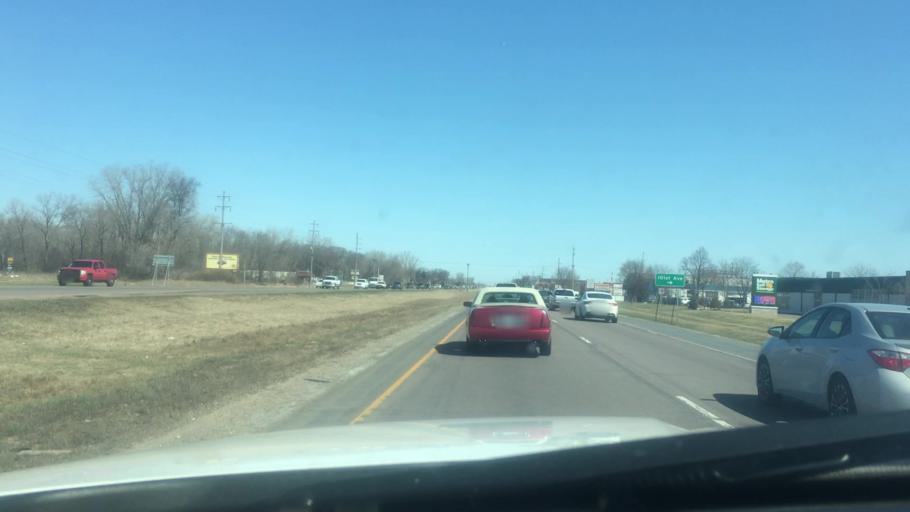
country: US
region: Minnesota
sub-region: Anoka County
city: Blaine
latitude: 45.1508
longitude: -93.2350
